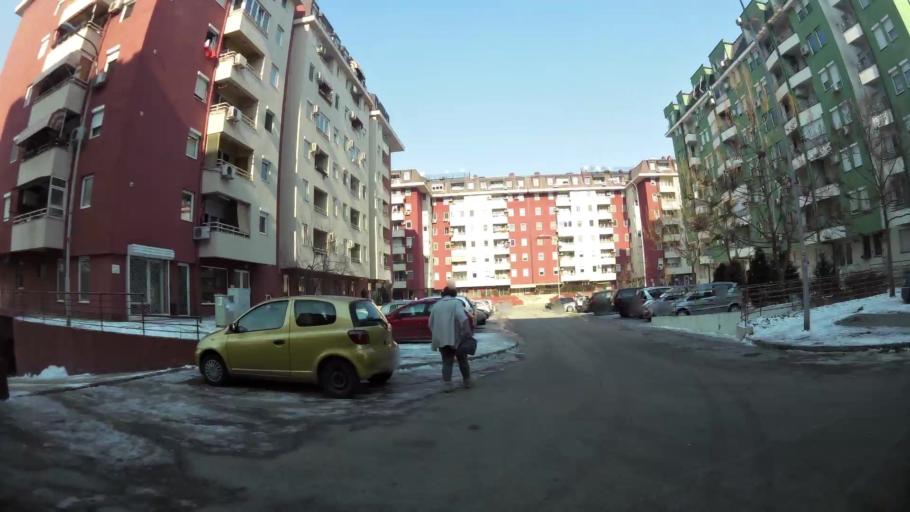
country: MK
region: Kisela Voda
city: Usje
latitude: 41.9751
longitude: 21.4454
